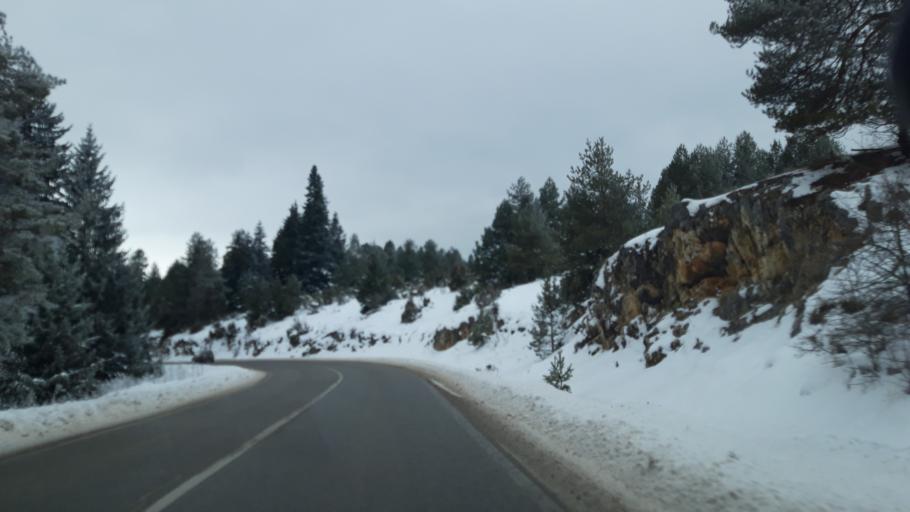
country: BA
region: Republika Srpska
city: Sokolac
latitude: 43.9920
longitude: 18.8746
